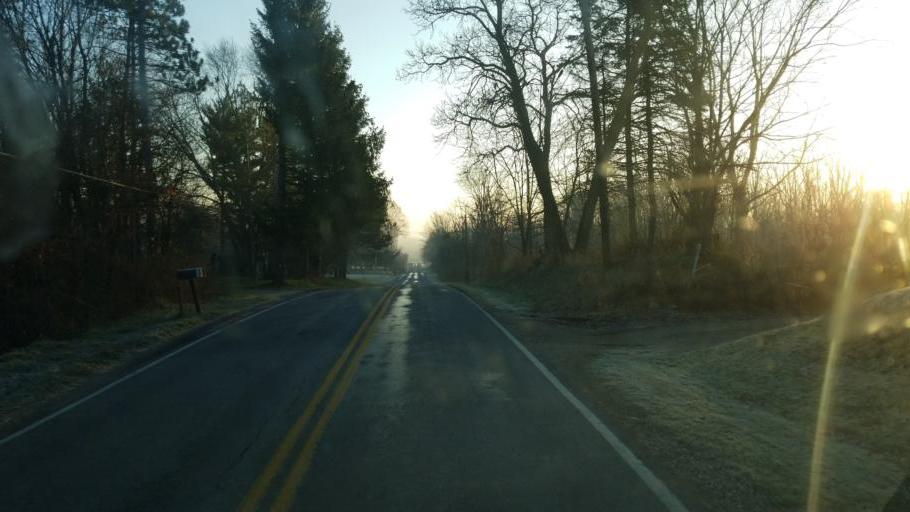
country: US
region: Ohio
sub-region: Medina County
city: Westfield Center
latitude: 41.0408
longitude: -81.9191
